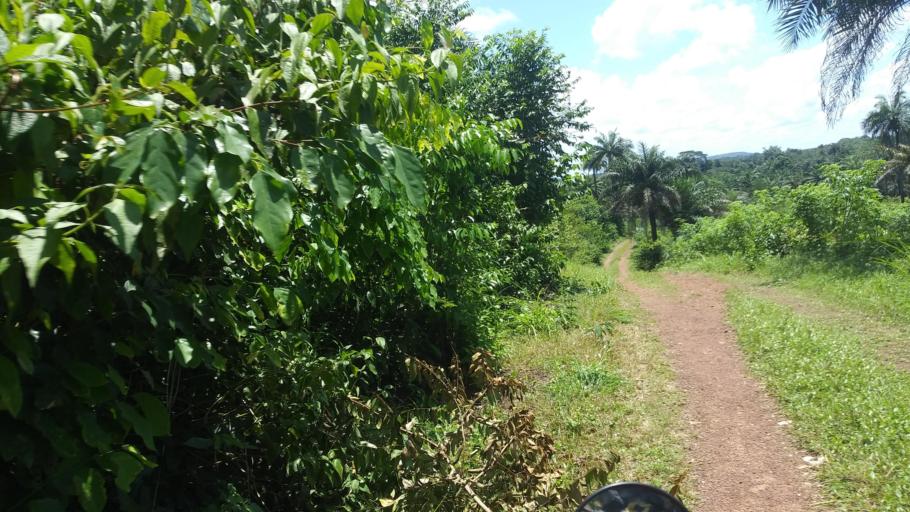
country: SL
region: Northern Province
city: Binkolo
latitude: 8.9099
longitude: -11.9779
